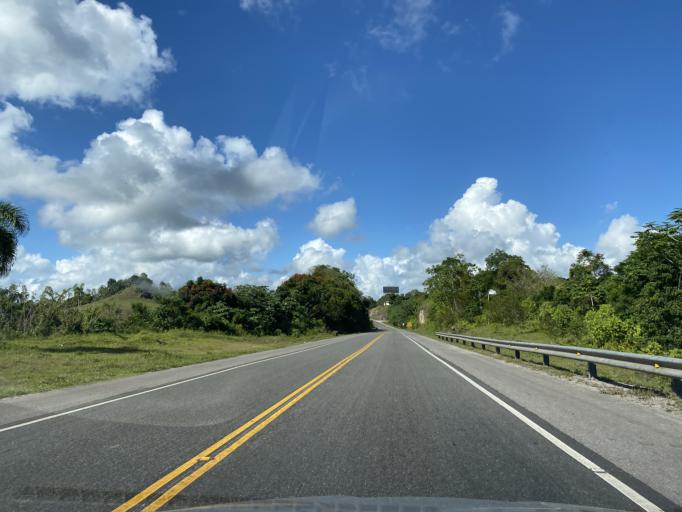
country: DO
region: Monte Plata
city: Majagual
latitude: 19.0382
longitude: -69.8280
